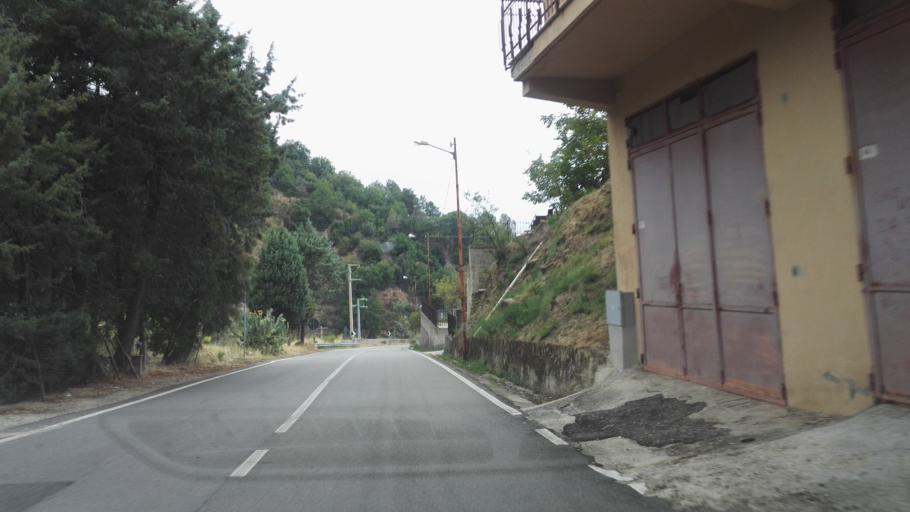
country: IT
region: Calabria
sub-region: Provincia di Catanzaro
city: Badolato
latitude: 38.5692
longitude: 16.5212
